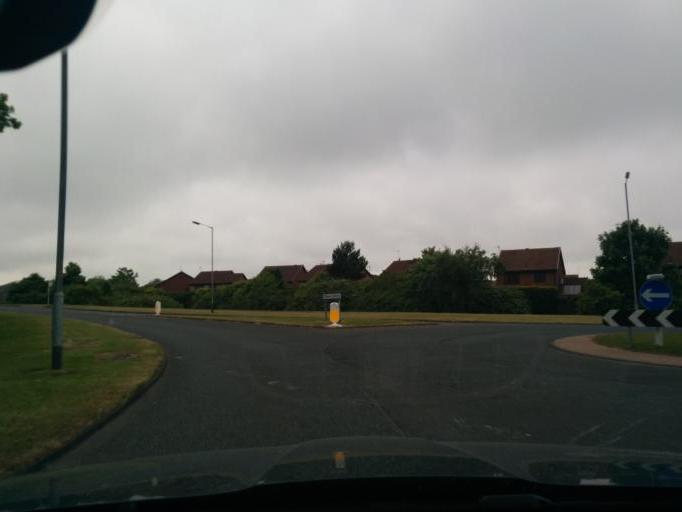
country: GB
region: England
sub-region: Northumberland
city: Cramlington
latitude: 55.0984
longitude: -1.5759
